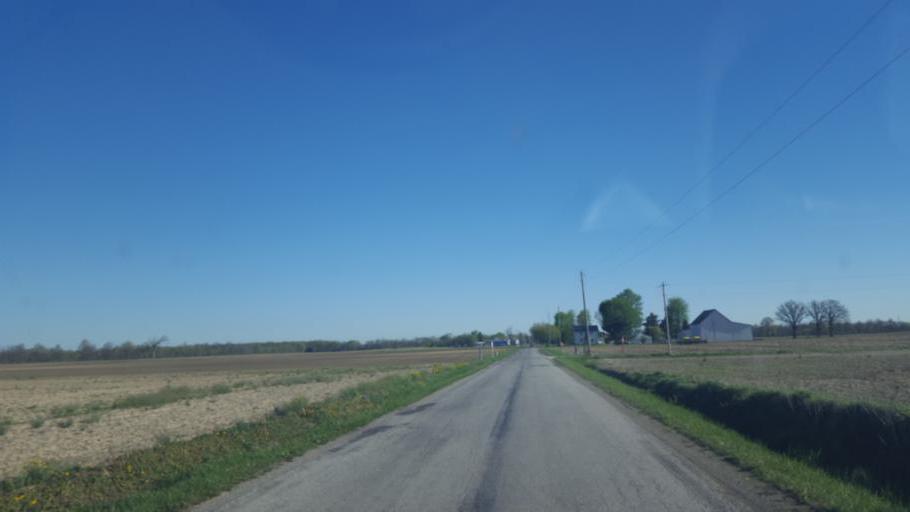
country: US
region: Ohio
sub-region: Morrow County
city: Mount Gilead
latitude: 40.6271
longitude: -82.9183
